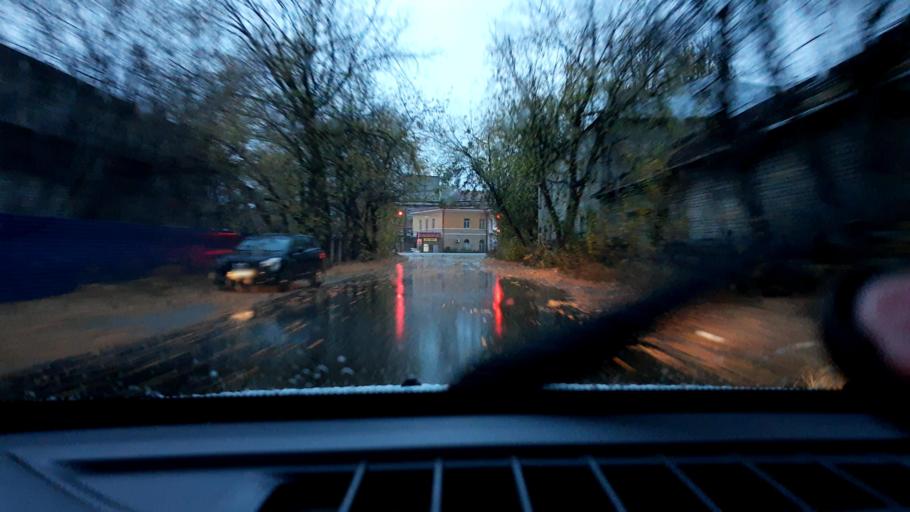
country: RU
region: Nizjnij Novgorod
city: Gorbatovka
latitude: 56.3403
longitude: 43.8191
